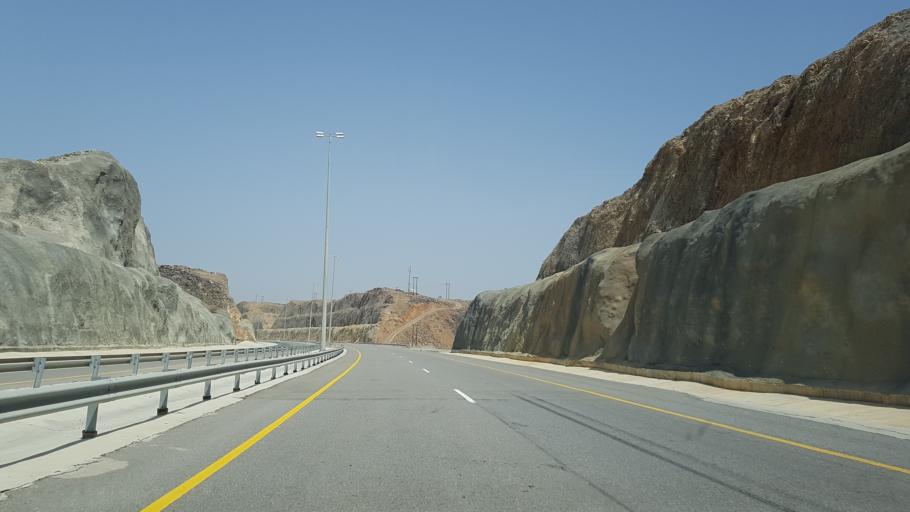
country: OM
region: Muhafazat Masqat
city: Muscat
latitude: 23.1885
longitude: 58.8571
